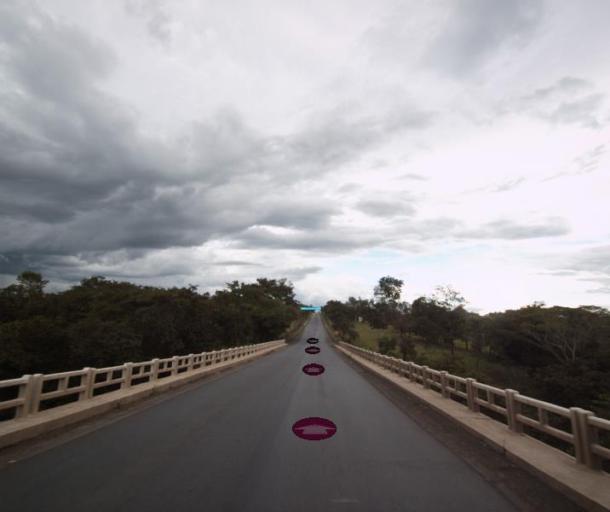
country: BR
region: Goias
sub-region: Itapaci
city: Itapaci
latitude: -15.0022
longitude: -49.4124
